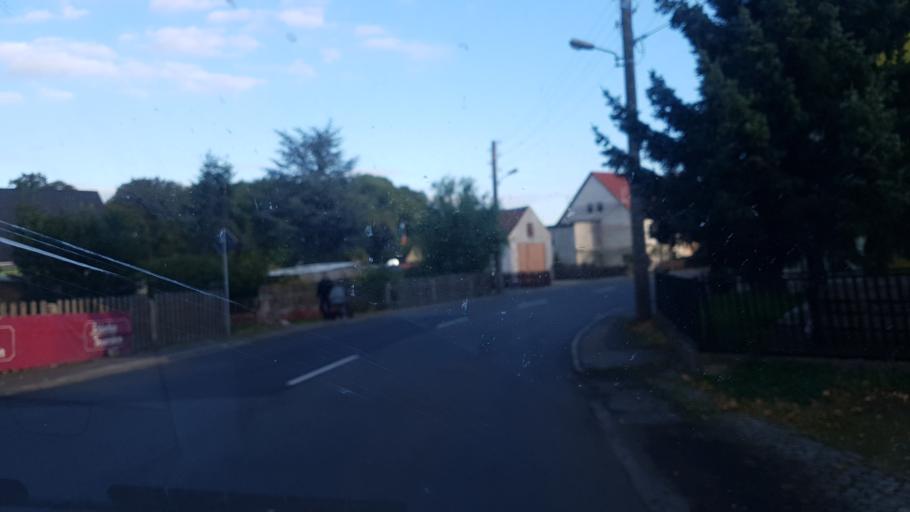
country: DE
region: Saxony
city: Dahlen
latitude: 51.3377
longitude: 13.0337
